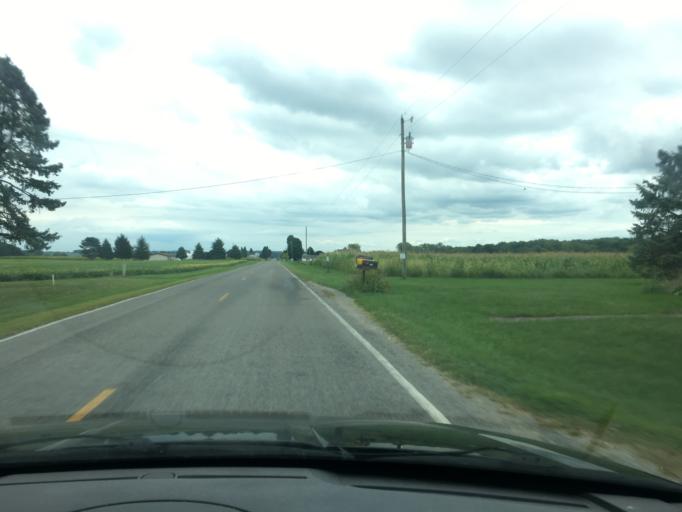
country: US
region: Ohio
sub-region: Logan County
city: West Liberty
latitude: 40.1927
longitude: -83.7655
